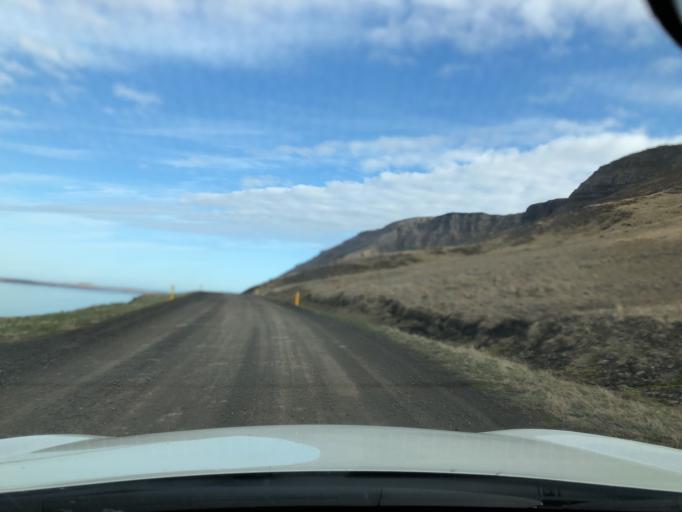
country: IS
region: West
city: Stykkisholmur
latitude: 64.9828
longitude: -22.5811
